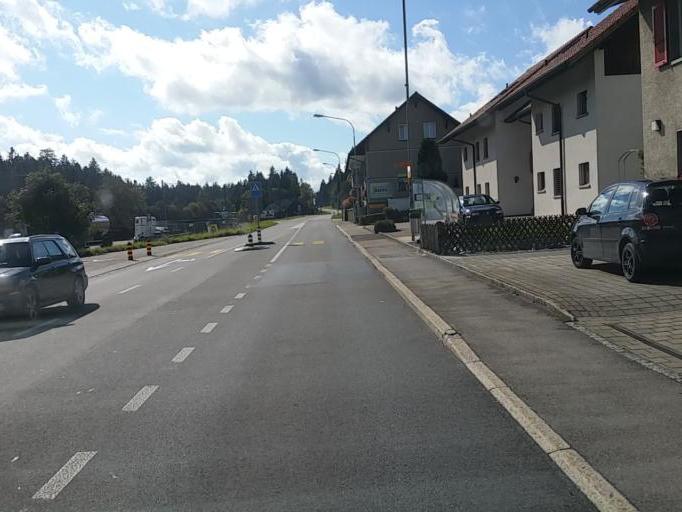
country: CH
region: Bern
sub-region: Emmental District
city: Durrenroth
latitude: 47.0789
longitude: 7.7491
